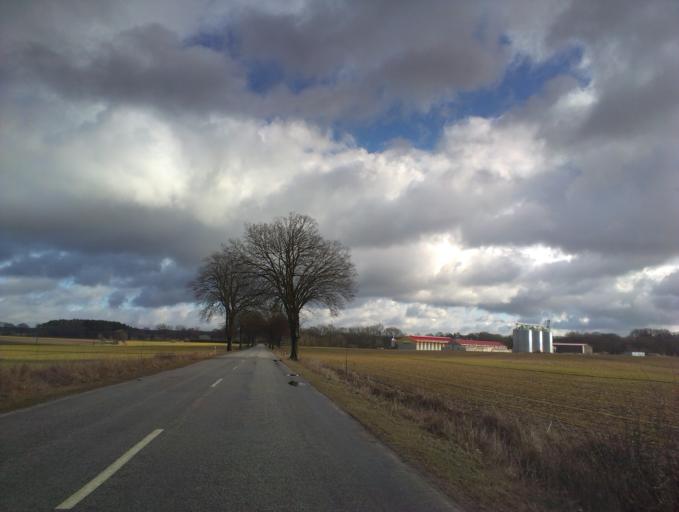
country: PL
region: Pomeranian Voivodeship
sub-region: Powiat czluchowski
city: Czarne
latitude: 53.6888
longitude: 17.0272
